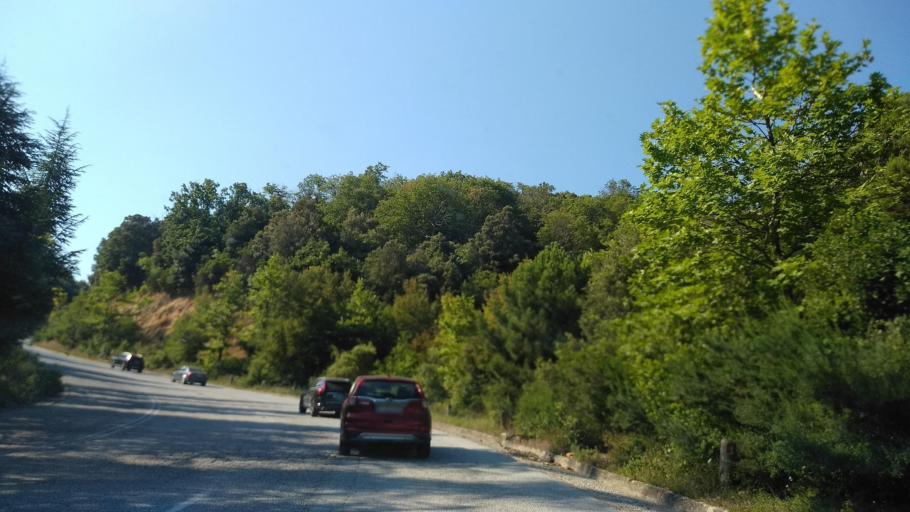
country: GR
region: Central Macedonia
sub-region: Nomos Chalkidikis
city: Stratonion
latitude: 40.5333
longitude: 23.8282
